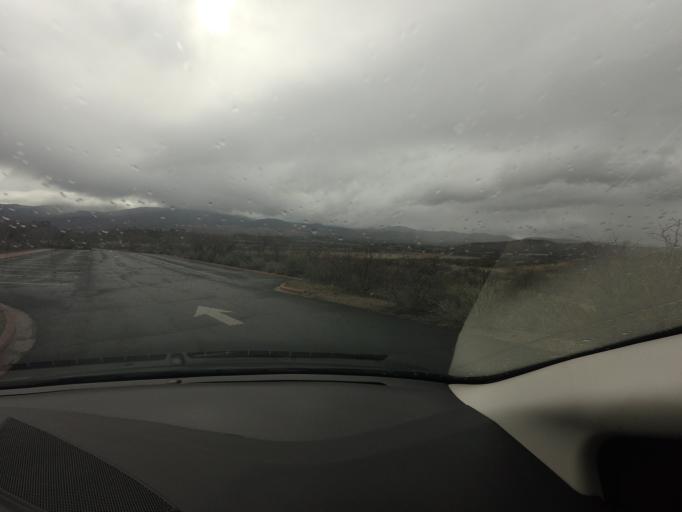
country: US
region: Arizona
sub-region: Yavapai County
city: Clarkdale
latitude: 34.7708
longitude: -112.0268
